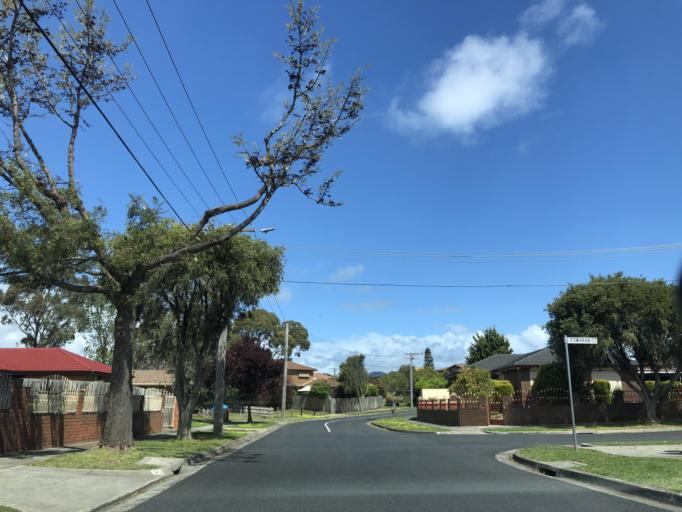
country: AU
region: Victoria
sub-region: Monash
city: Oakleigh South
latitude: -37.9337
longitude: 145.0961
